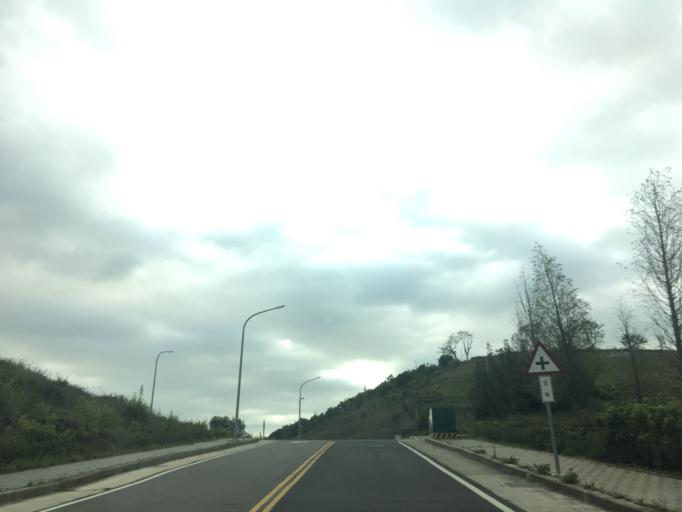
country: TW
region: Taiwan
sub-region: Taichung City
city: Taichung
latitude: 24.1718
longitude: 120.7696
